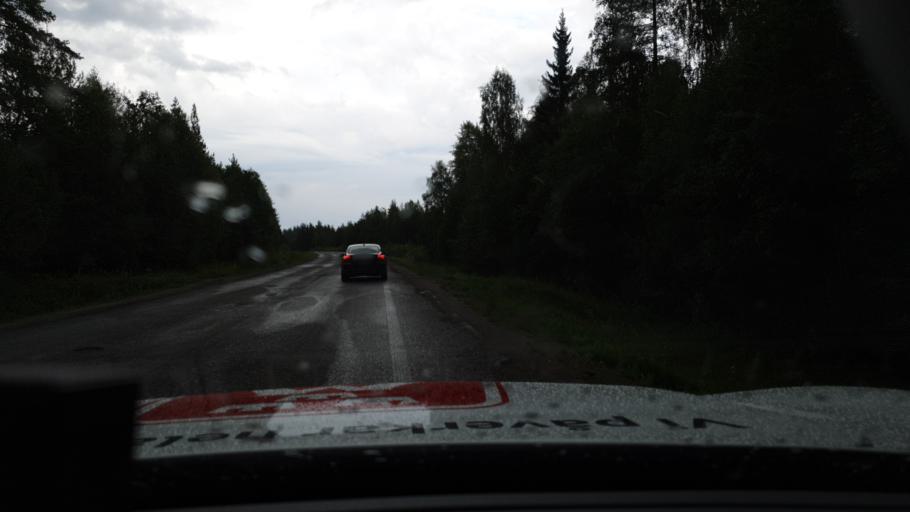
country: SE
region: Norrbotten
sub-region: Bodens Kommun
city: Boden
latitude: 65.8497
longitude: 21.5357
